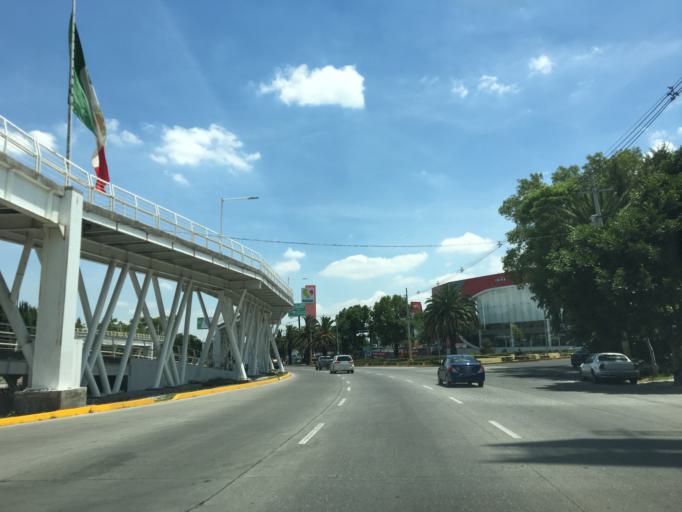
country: MX
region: Puebla
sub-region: Cuautlancingo
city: Sanctorum
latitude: 19.0773
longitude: -98.2277
